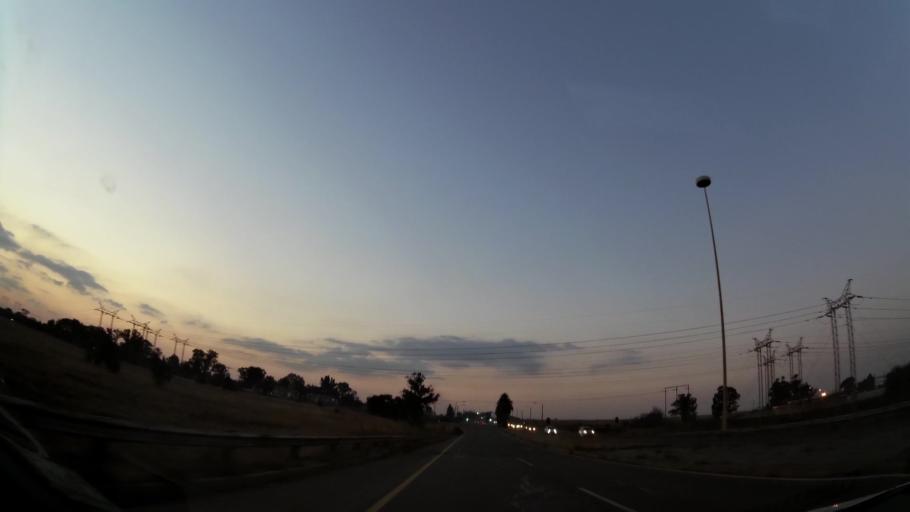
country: ZA
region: Gauteng
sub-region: Ekurhuleni Metropolitan Municipality
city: Springs
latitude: -26.3181
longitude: 28.4555
